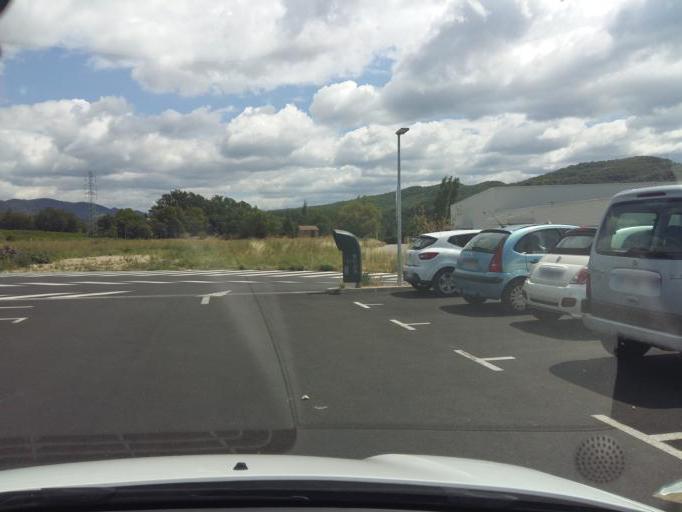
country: FR
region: Provence-Alpes-Cote d'Azur
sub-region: Departement du Vaucluse
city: Vaison-la-Romaine
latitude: 44.2557
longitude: 5.0971
